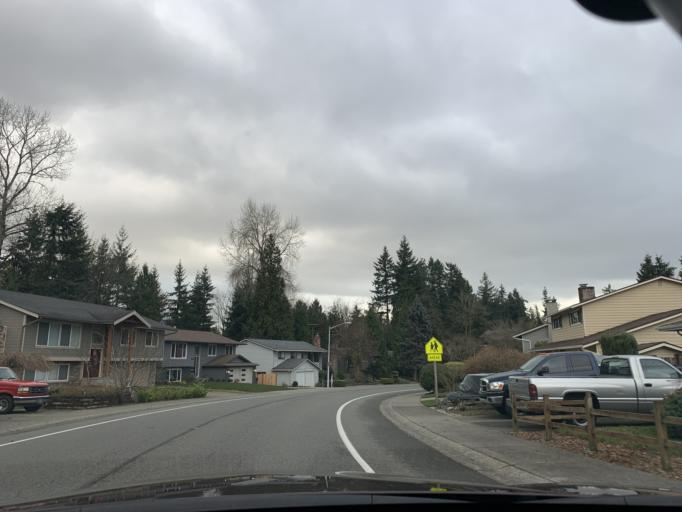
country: US
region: Washington
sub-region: King County
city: Kingsgate
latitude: 47.7430
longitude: -122.1816
